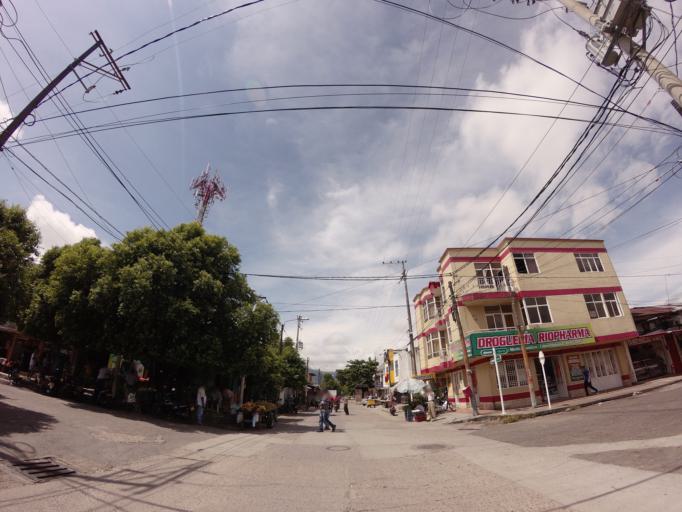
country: CO
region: Caldas
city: La Dorada
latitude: 5.4531
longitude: -74.6661
